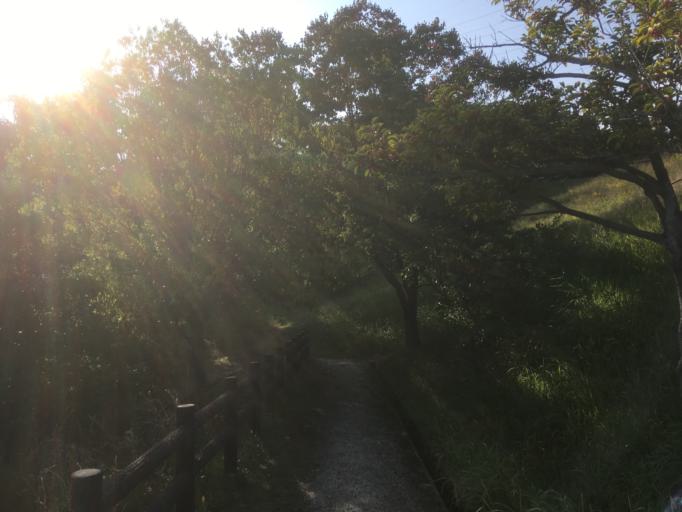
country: JP
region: Nara
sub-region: Ikoma-shi
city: Ikoma
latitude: 34.7288
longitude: 135.7139
